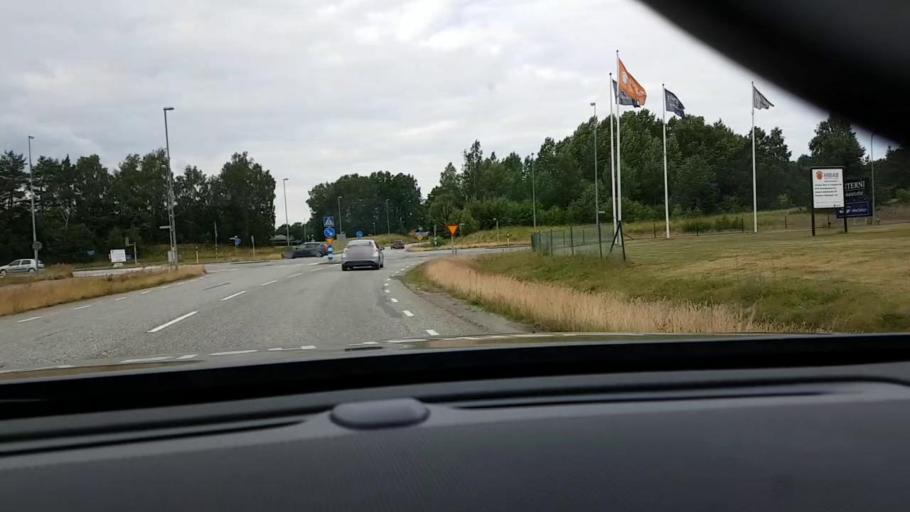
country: SE
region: Skane
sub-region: Hassleholms Kommun
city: Hassleholm
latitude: 56.1686
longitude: 13.8017
